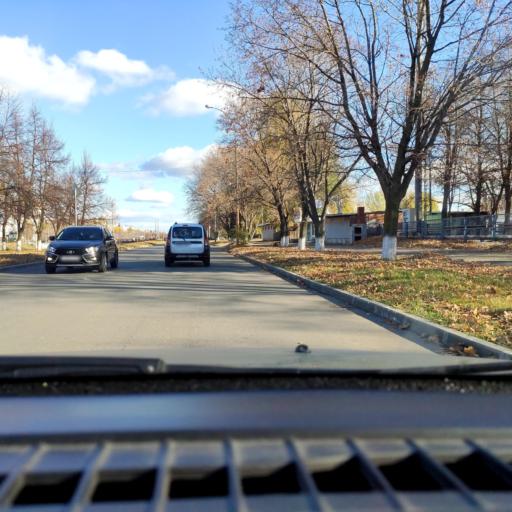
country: RU
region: Samara
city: Tol'yatti
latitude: 53.5203
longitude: 49.2690
